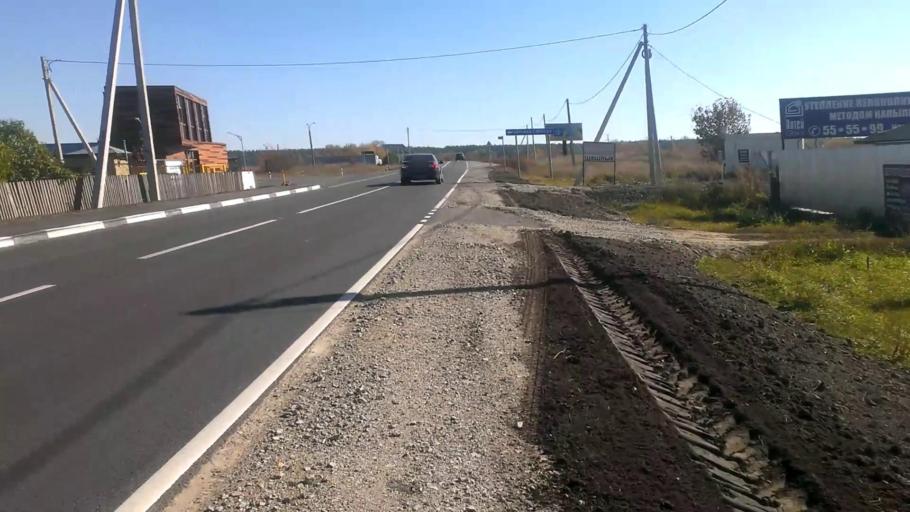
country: RU
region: Altai Krai
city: Sannikovo
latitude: 53.3142
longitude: 83.9612
